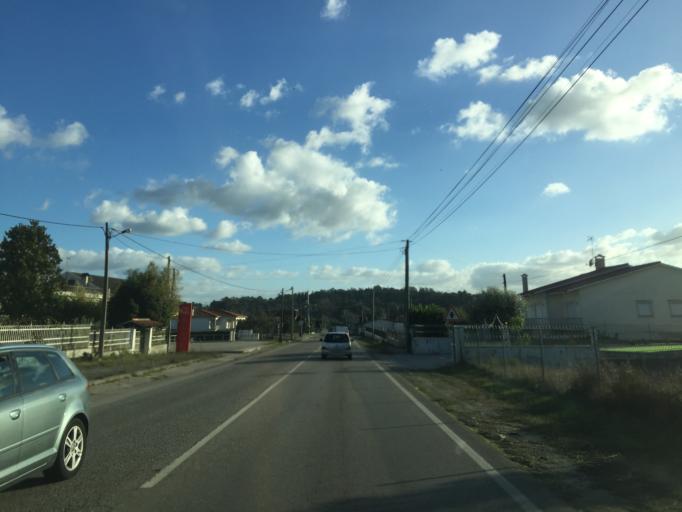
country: PT
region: Leiria
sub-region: Leiria
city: Souto da Carpalhosa
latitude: 39.8684
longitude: -8.8392
